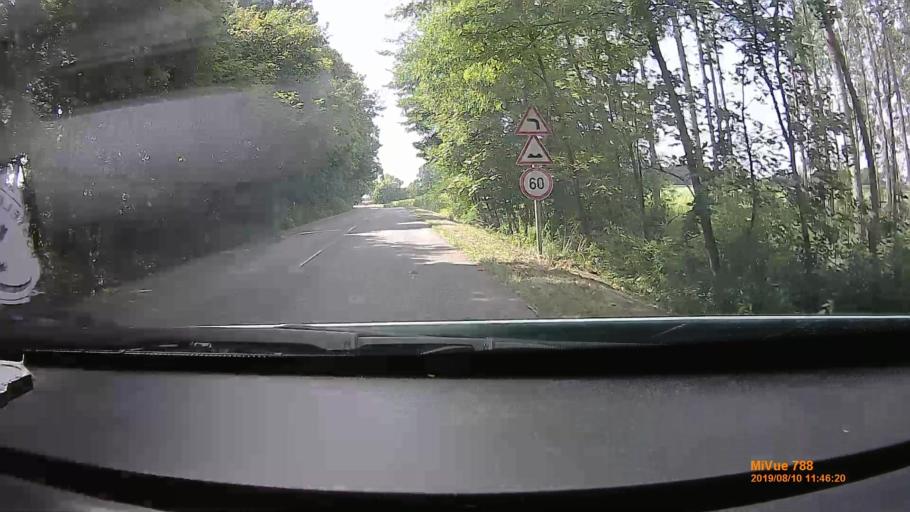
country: HU
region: Borsod-Abauj-Zemplen
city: Szentistvan
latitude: 47.7119
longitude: 20.6322
